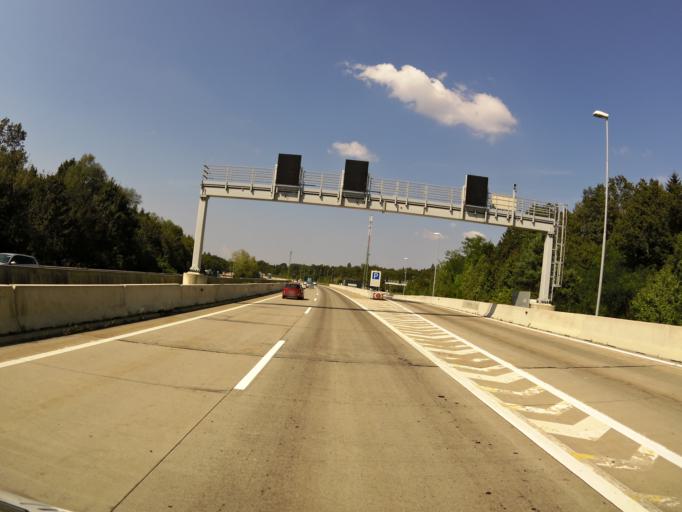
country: AT
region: Styria
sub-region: Politischer Bezirk Leibnitz
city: Strass in Steiermark
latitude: 46.7290
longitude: 15.6447
